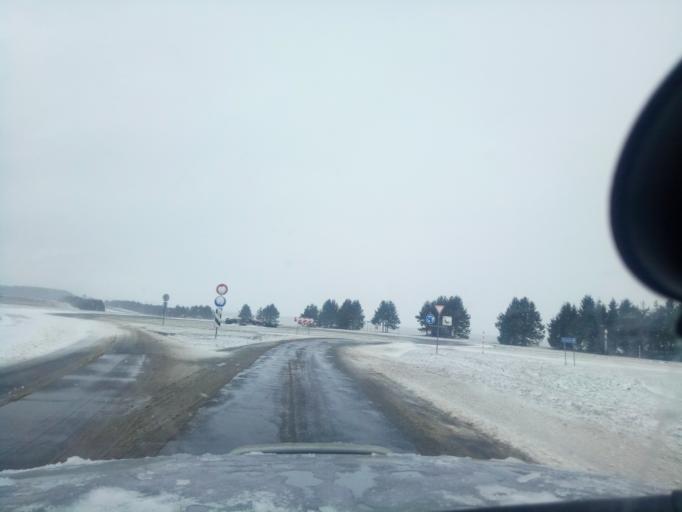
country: BY
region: Minsk
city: Haradzyeya
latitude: 53.2947
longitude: 26.5750
